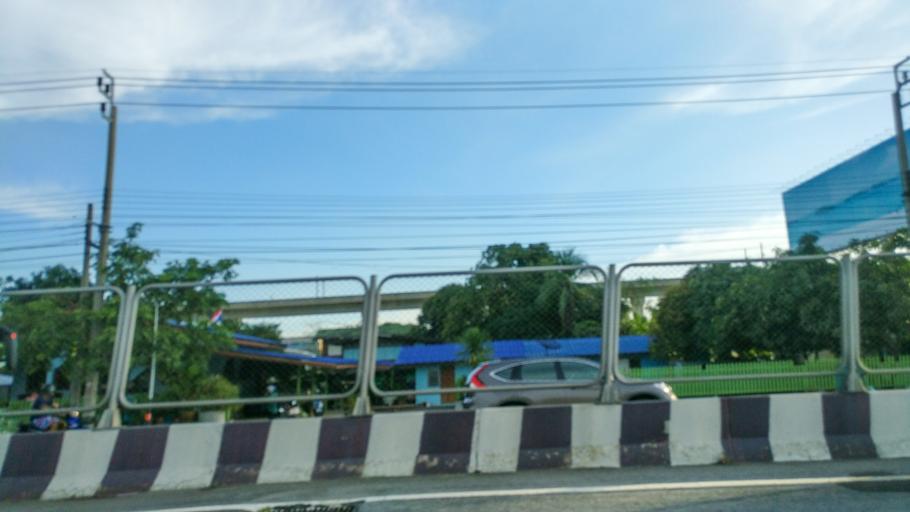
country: TH
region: Bangkok
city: Lat Krabang
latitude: 13.7295
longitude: 100.7521
